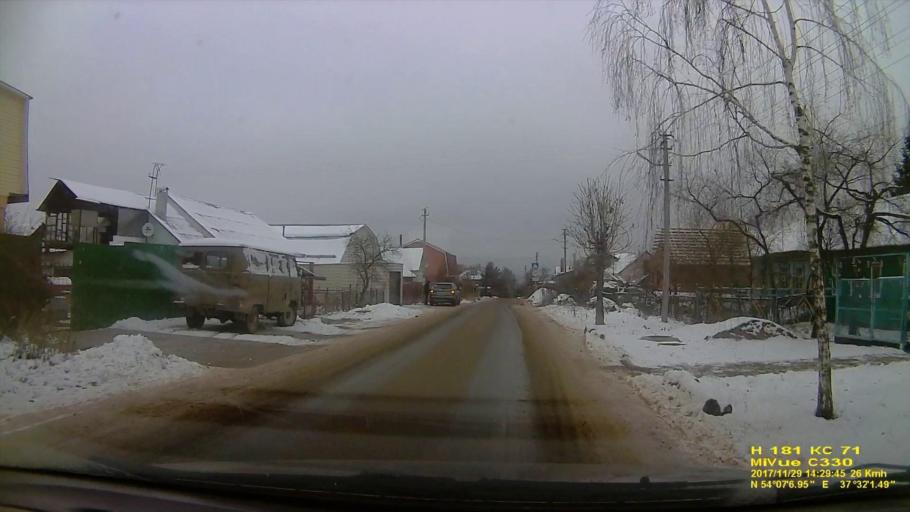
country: RU
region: Tula
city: Kosaya Gora
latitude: 54.1187
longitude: 37.5338
